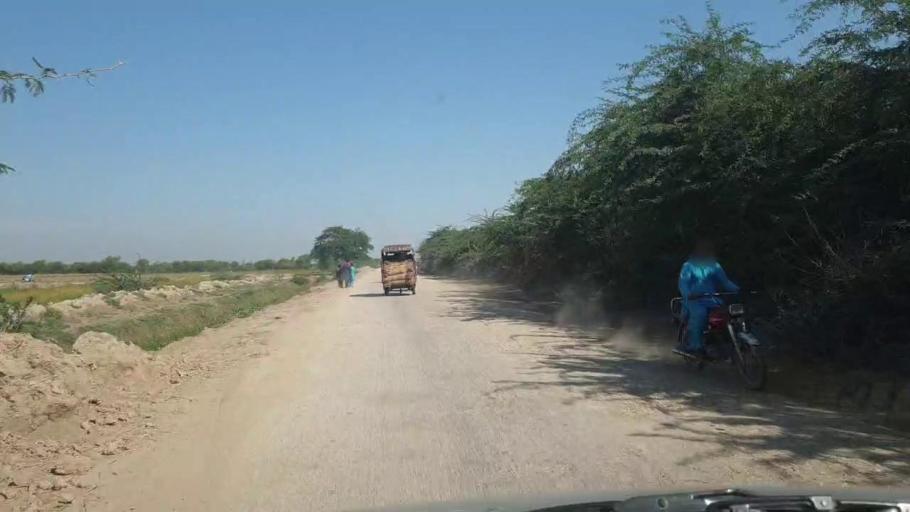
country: PK
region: Sindh
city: Tando Bago
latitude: 24.8037
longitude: 68.9786
